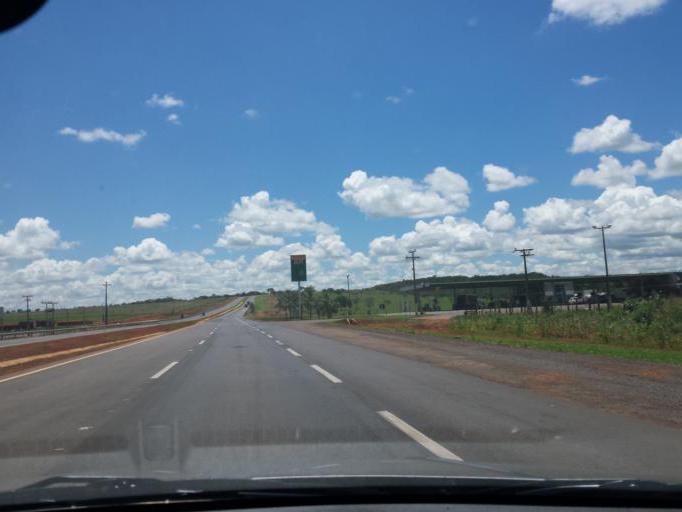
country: BR
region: Goias
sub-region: Cristalina
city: Cristalina
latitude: -16.6205
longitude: -47.7503
